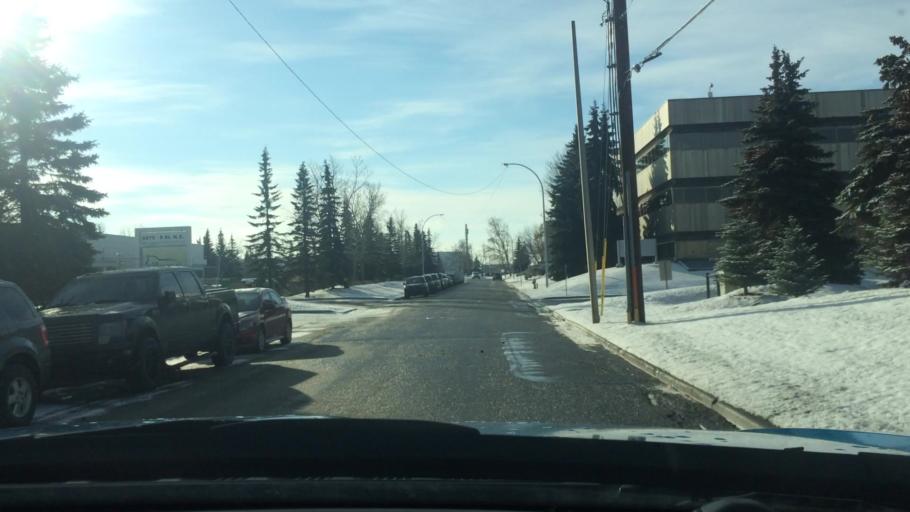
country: CA
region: Alberta
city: Calgary
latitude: 51.1149
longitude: -114.0446
